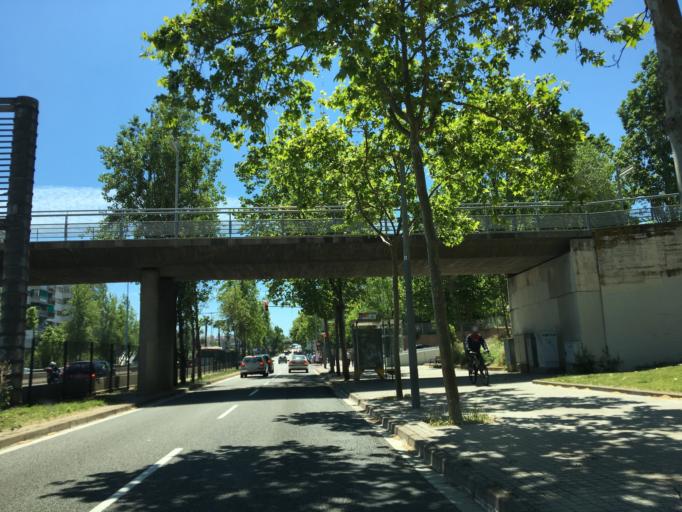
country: ES
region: Catalonia
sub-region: Provincia de Barcelona
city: Horta-Guinardo
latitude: 41.4323
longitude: 2.1456
